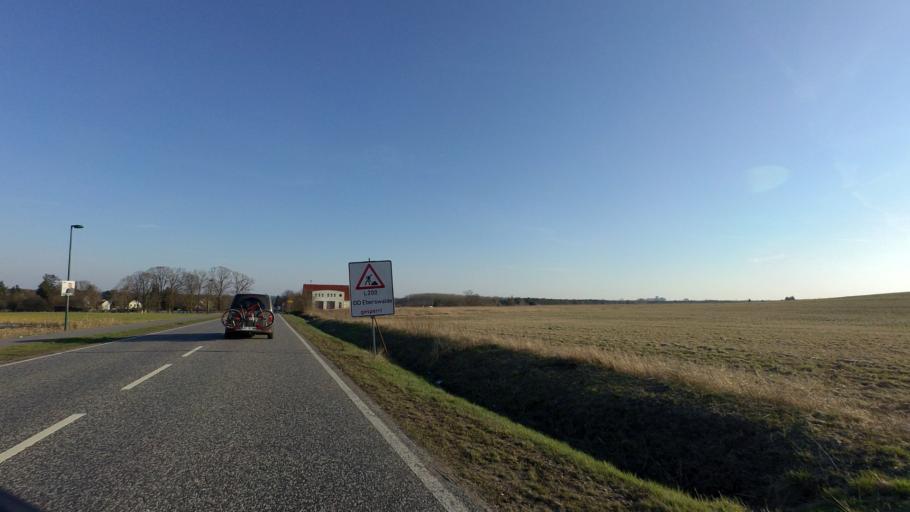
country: DE
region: Brandenburg
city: Britz
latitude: 52.8821
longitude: 13.8154
